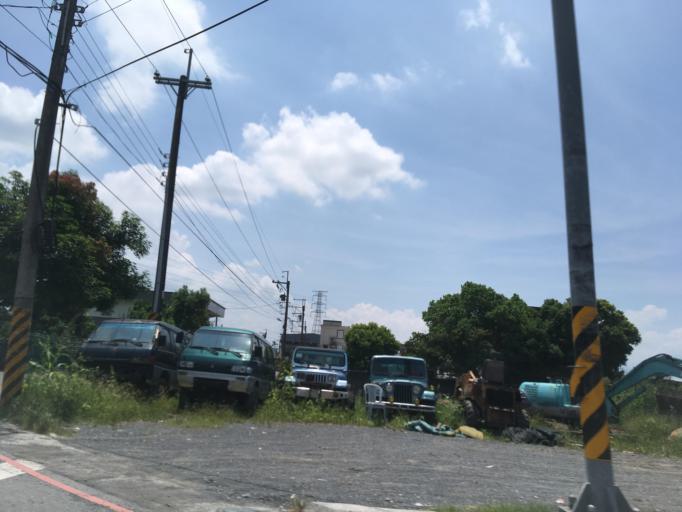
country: TW
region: Taiwan
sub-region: Yilan
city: Yilan
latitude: 24.6610
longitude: 121.7609
